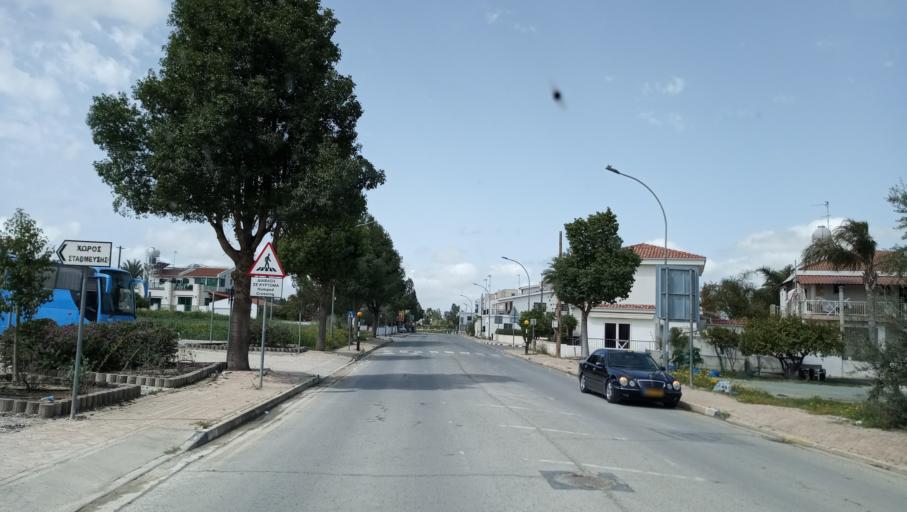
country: CY
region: Lefkosia
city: Dali
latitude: 35.0195
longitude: 33.4224
